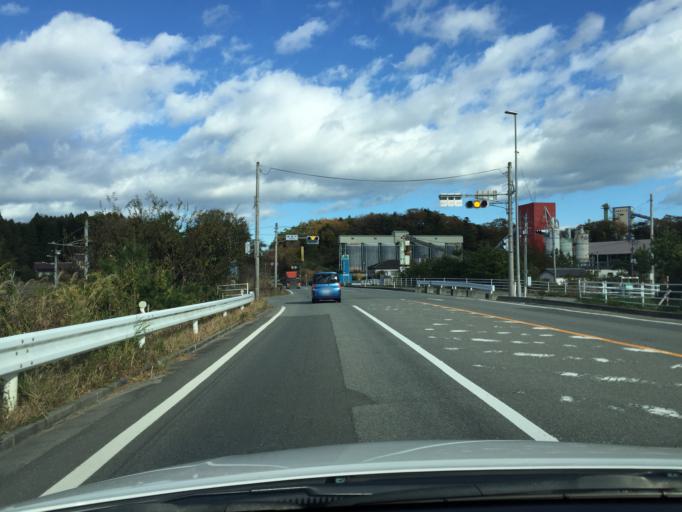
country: JP
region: Fukushima
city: Namie
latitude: 37.4342
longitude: 141.0109
